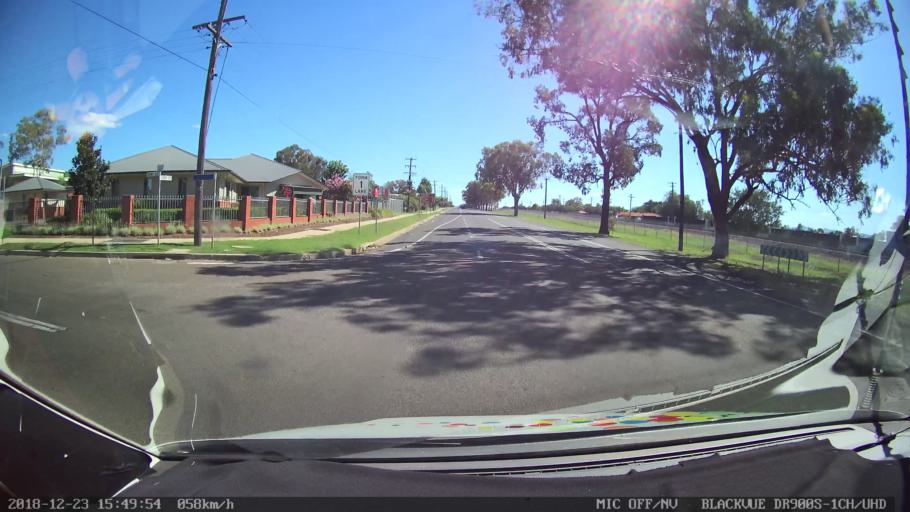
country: AU
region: New South Wales
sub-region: Tamworth Municipality
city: South Tamworth
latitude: -31.1024
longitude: 150.9036
